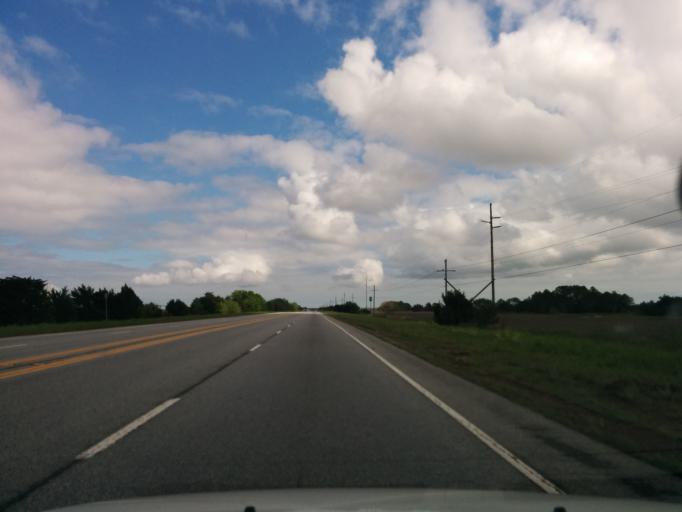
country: US
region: Georgia
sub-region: Glynn County
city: Brunswick
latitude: 31.1109
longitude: -81.5212
